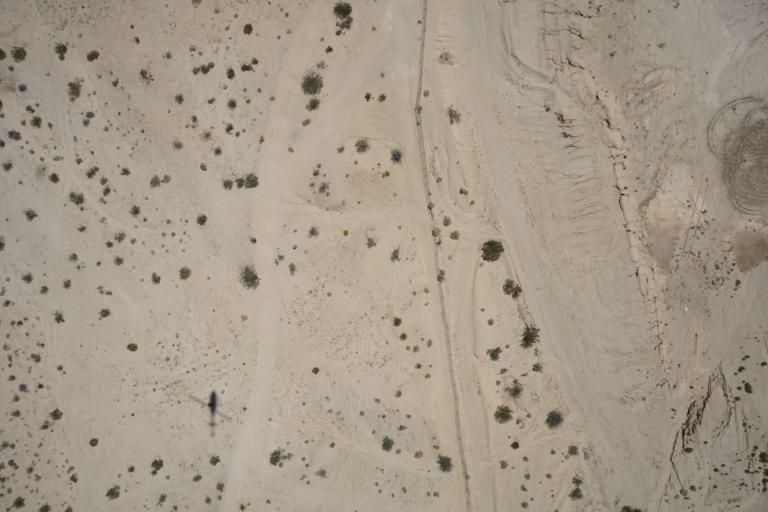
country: US
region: California
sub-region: San Bernardino County
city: Twentynine Palms
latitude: 34.1389
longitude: -116.0653
